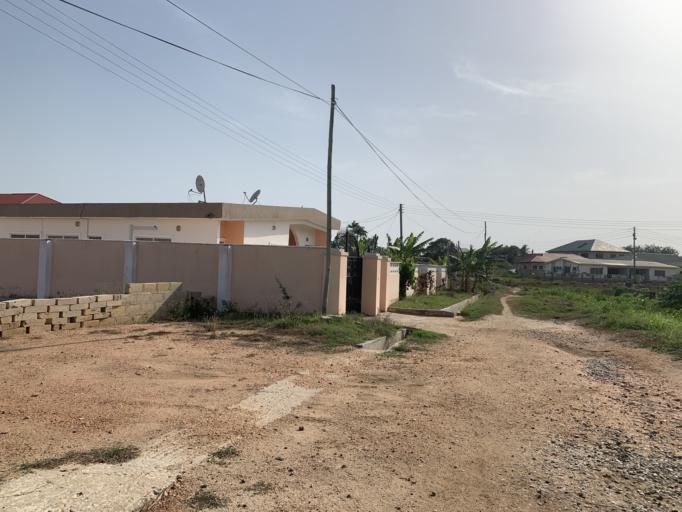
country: GH
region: Central
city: Winneba
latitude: 5.3671
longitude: -0.6412
